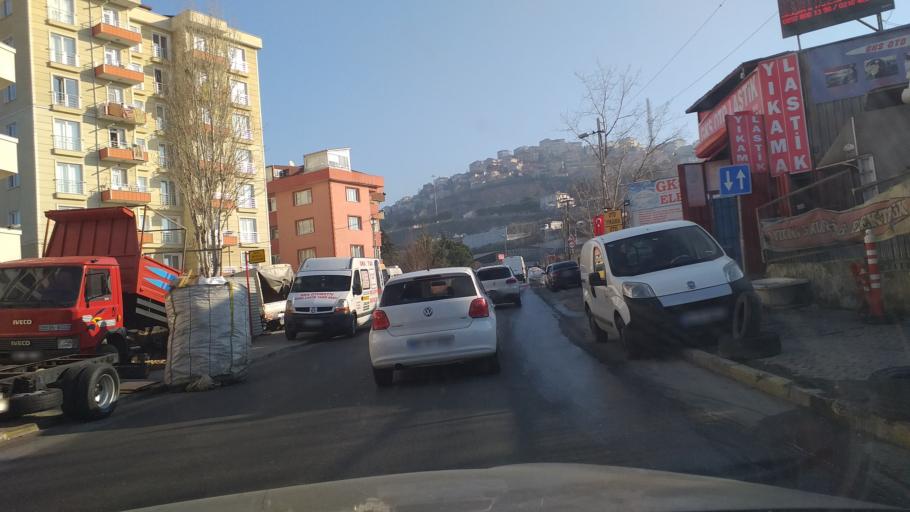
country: TR
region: Istanbul
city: Maltepe
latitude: 40.9319
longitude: 29.1513
